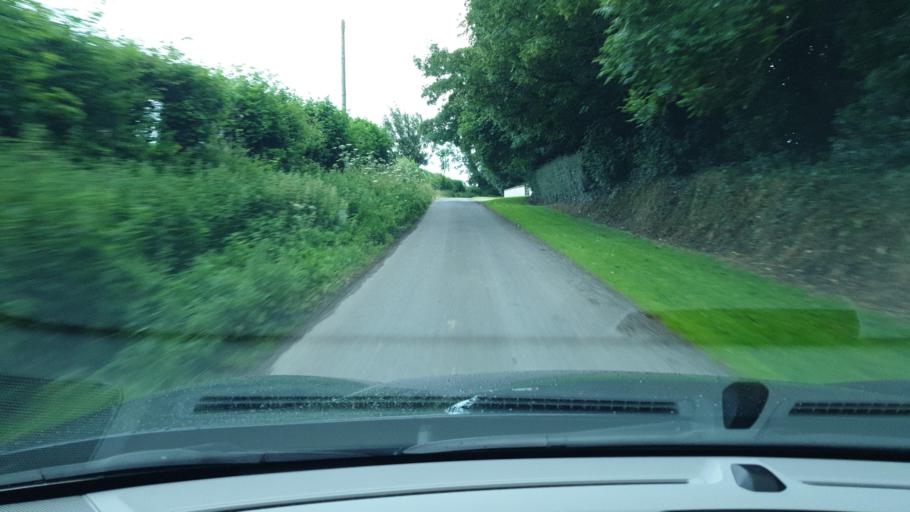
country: IE
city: Kentstown
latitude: 53.5911
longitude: -6.5669
